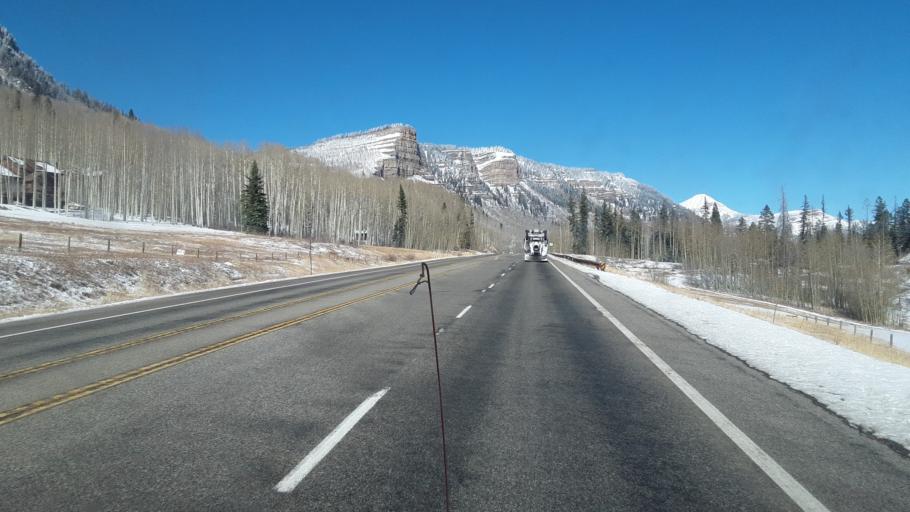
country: US
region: Colorado
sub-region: San Juan County
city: Silverton
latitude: 37.5789
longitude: -107.8228
